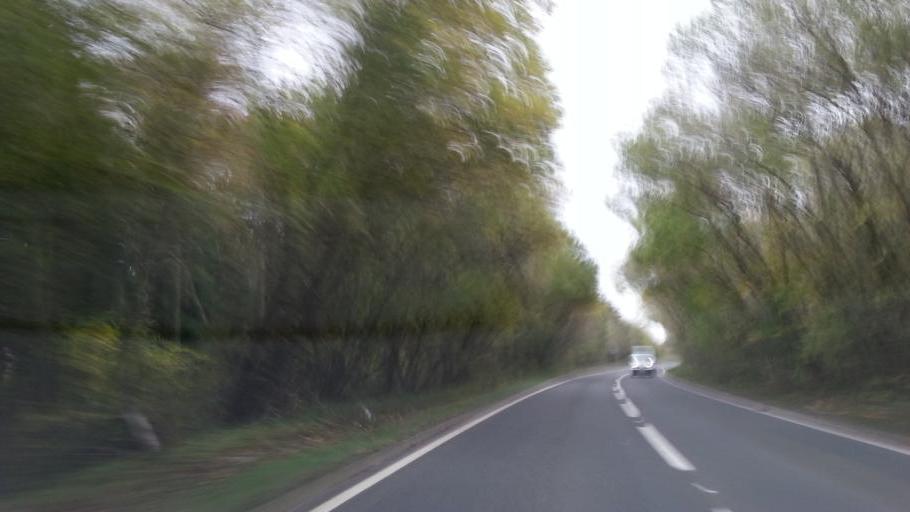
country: GB
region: England
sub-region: Northamptonshire
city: Corby
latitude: 52.4958
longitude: -0.7396
